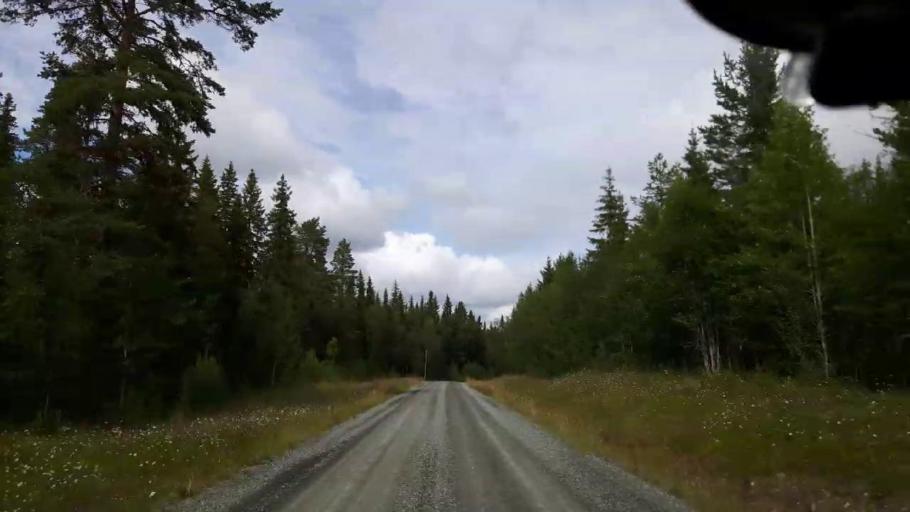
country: SE
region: Jaemtland
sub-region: Krokoms Kommun
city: Valla
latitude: 63.5473
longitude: 13.9164
